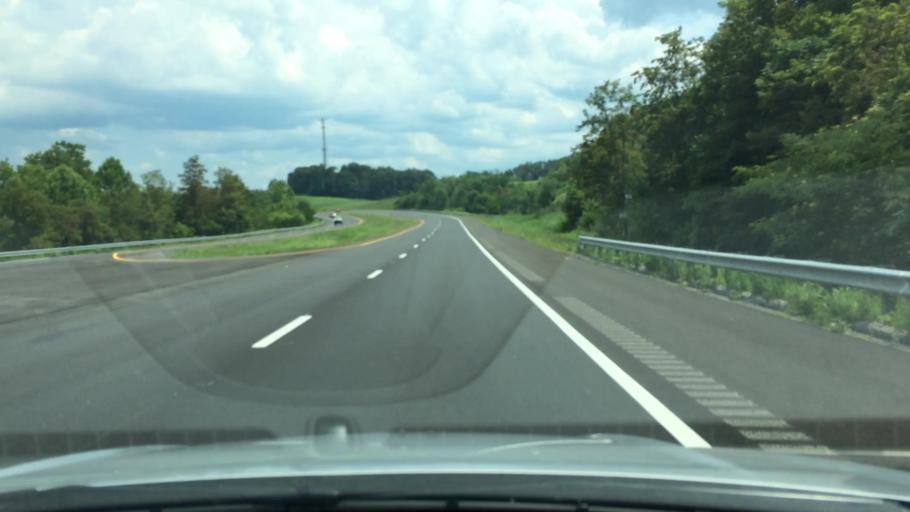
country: US
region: Tennessee
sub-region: Hamblen County
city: Morristown
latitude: 36.1750
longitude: -83.2315
